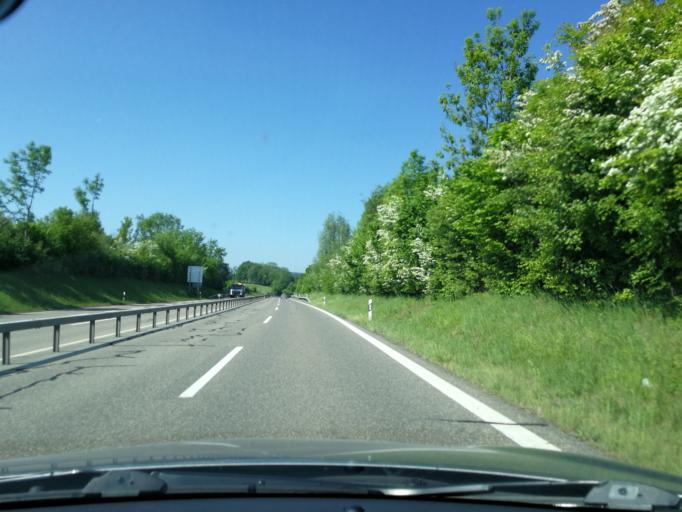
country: CH
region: Zurich
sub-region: Bezirk Hinwil
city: Gruet
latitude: 47.2915
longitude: 8.7805
